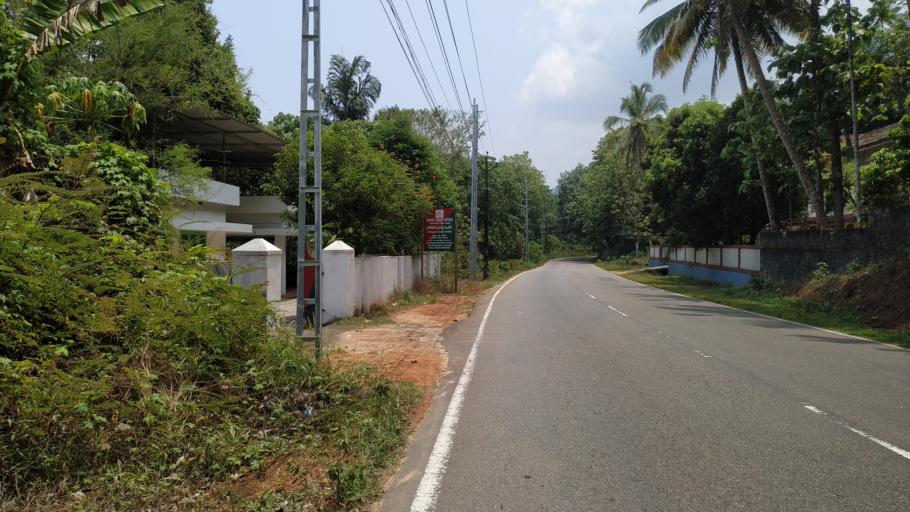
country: IN
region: Kerala
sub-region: Kottayam
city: Lalam
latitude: 9.8343
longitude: 76.7577
